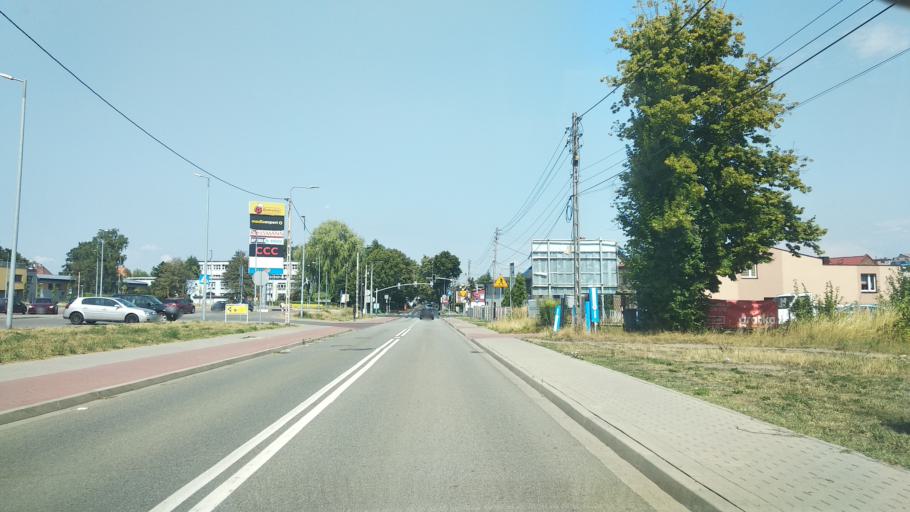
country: PL
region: Silesian Voivodeship
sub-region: Powiat tarnogorski
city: Radzionkow
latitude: 50.3952
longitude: 18.8959
